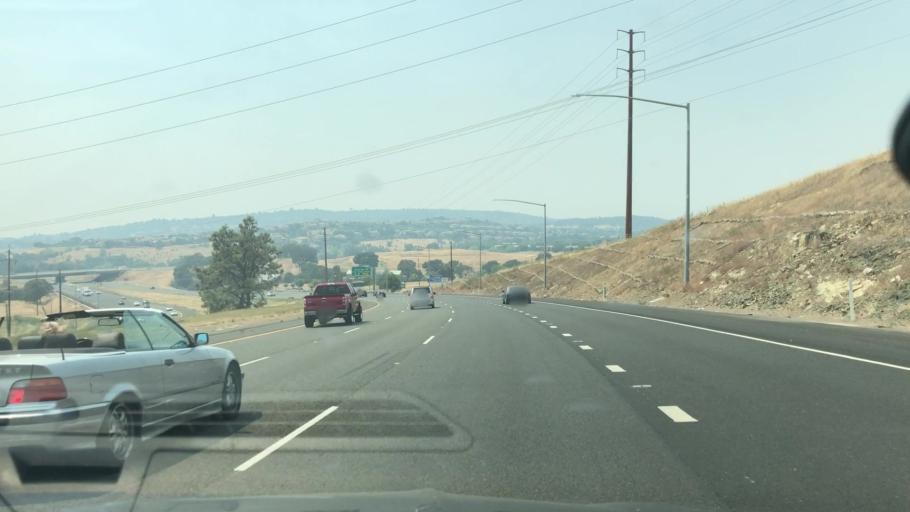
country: US
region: California
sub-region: El Dorado County
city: El Dorado Hills
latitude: 38.6579
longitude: -121.0457
